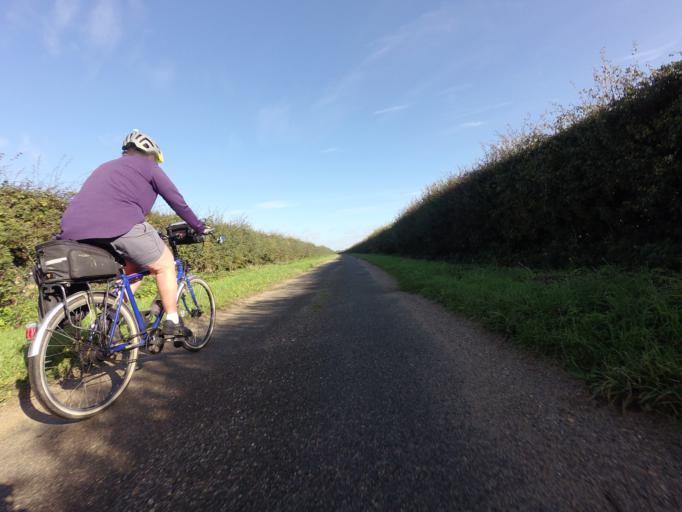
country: GB
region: England
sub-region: Norfolk
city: Dersingham
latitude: 52.8308
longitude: 0.6741
